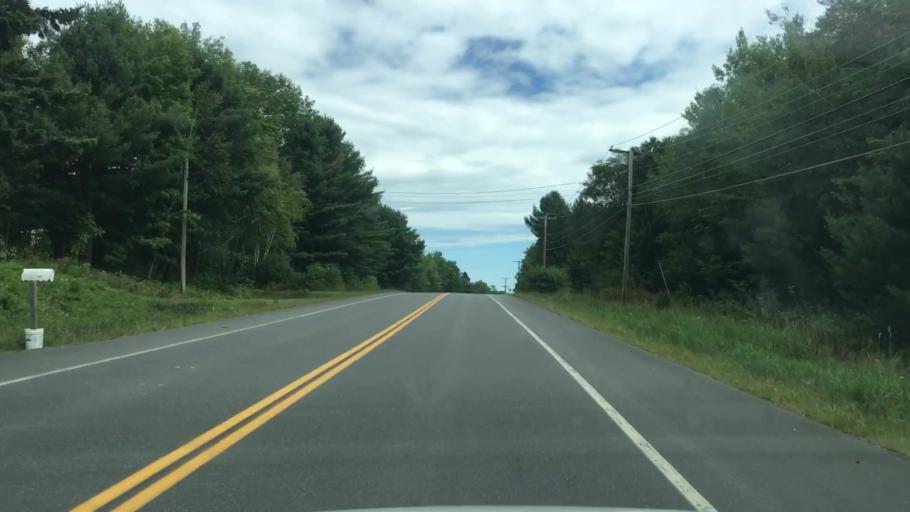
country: US
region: Maine
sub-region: Piscataquis County
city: Milo
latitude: 45.2428
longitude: -69.0185
